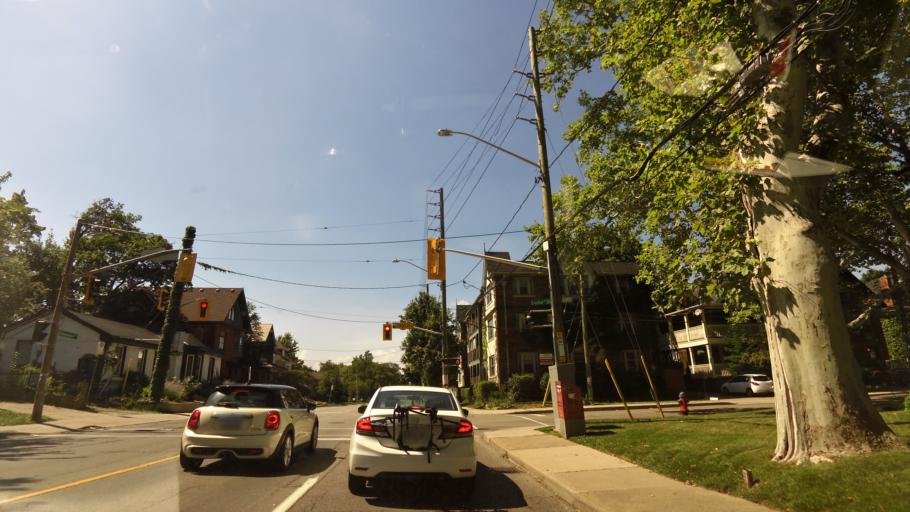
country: CA
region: Ontario
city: Hamilton
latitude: 43.2494
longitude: -79.8876
